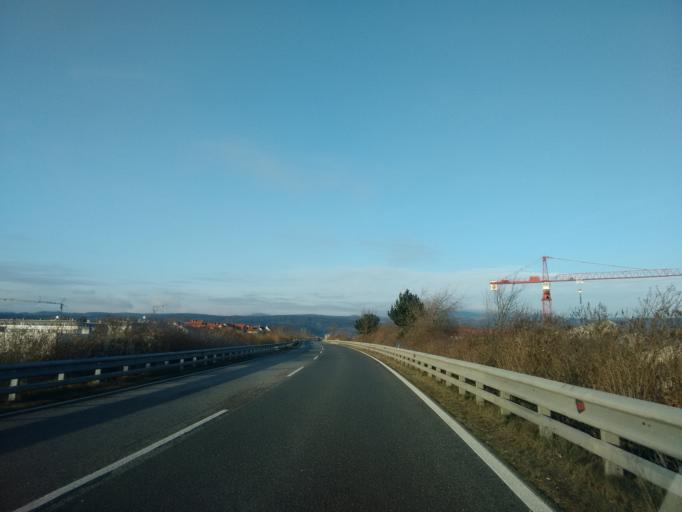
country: AT
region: Lower Austria
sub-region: Politischer Bezirk Melk
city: Melk
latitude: 48.2267
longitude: 15.3497
